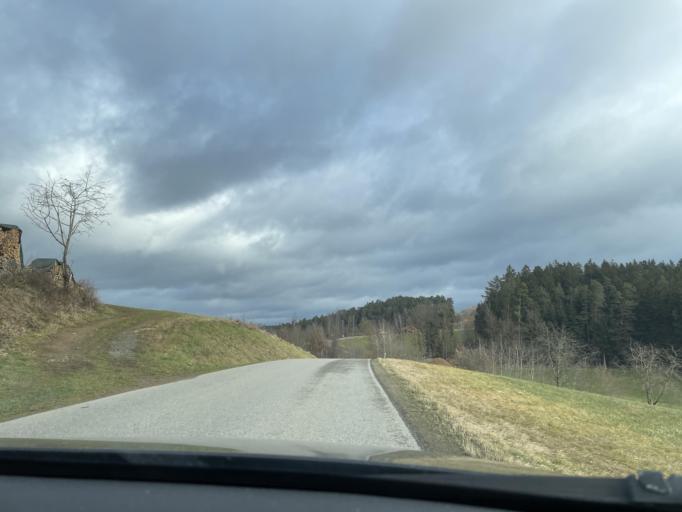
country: DE
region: Bavaria
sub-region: Lower Bavaria
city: Prackenbach
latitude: 49.1133
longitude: 12.8410
